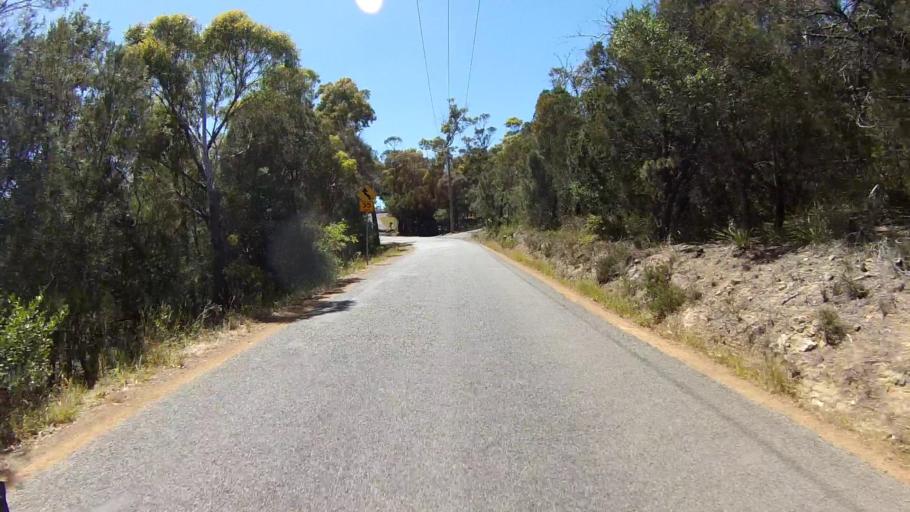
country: AU
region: Tasmania
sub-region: Clarence
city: Cambridge
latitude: -42.8547
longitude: 147.4221
